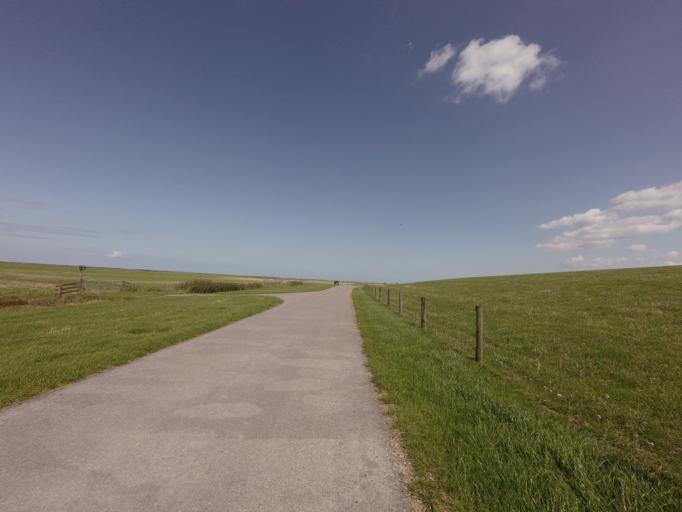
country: NL
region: Friesland
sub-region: Gemeente Ferwerderadiel
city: Marrum
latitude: 53.3403
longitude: 5.7886
